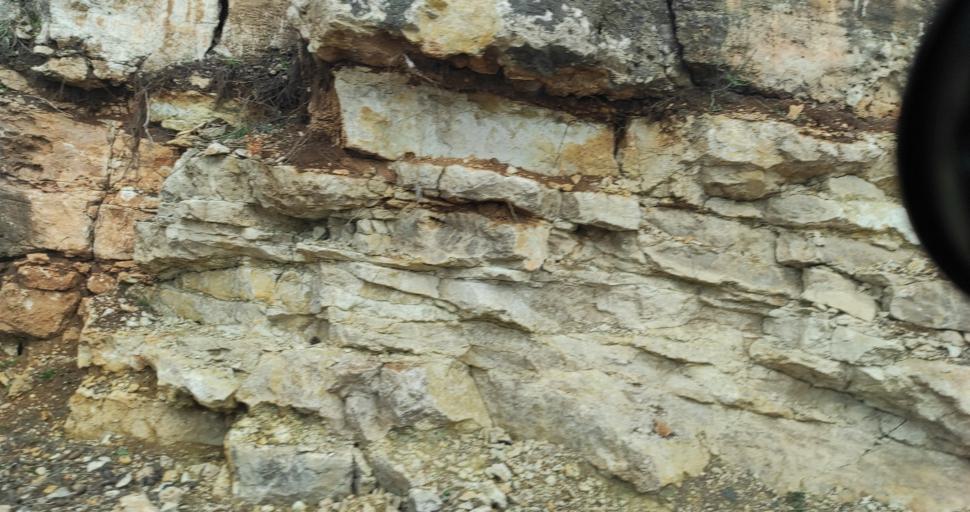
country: AL
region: Lezhe
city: Shengjin
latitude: 41.8171
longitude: 19.5678
